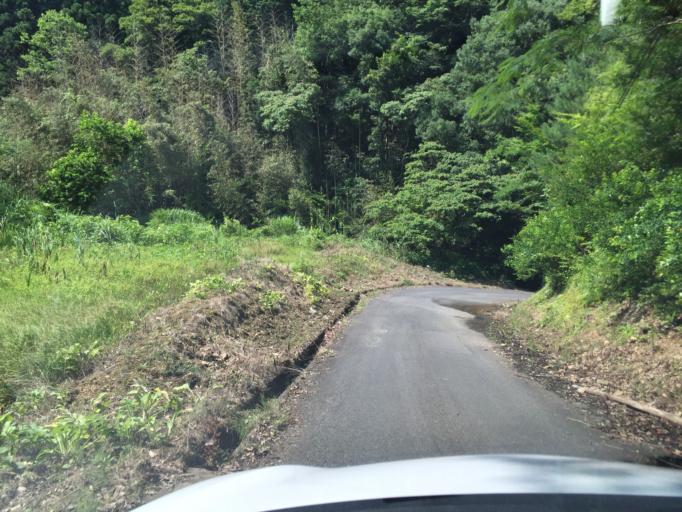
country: JP
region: Ibaraki
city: Kitaibaraki
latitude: 36.9353
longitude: 140.7290
